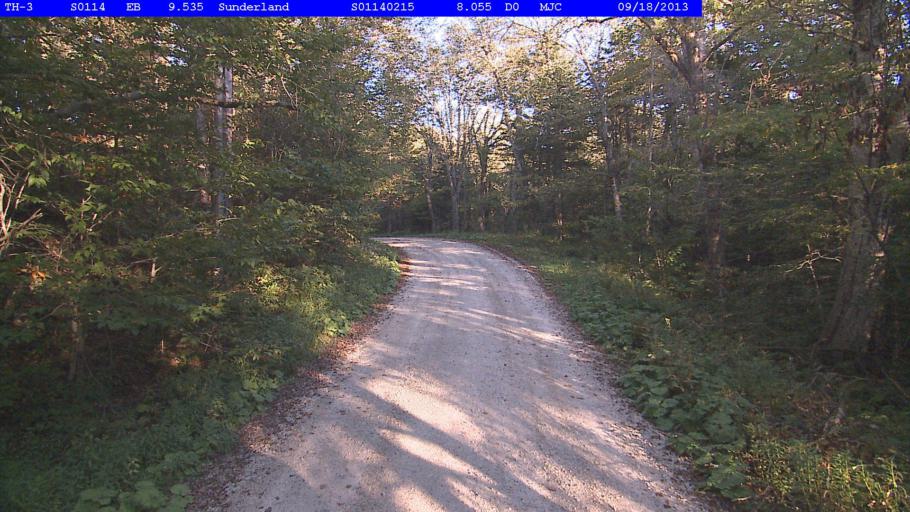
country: US
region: Vermont
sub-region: Bennington County
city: Manchester Center
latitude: 43.0548
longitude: -73.0304
